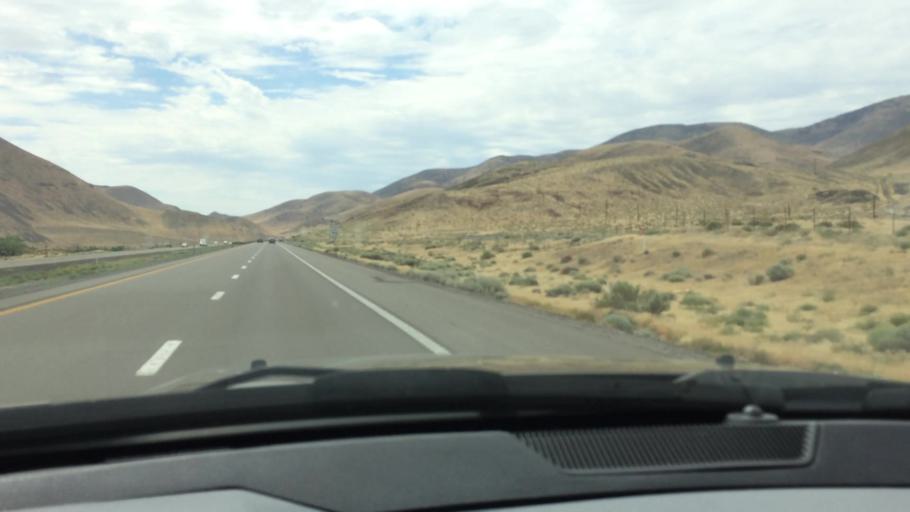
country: US
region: Nevada
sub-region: Lyon County
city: Fernley
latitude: 39.5894
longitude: -119.4348
